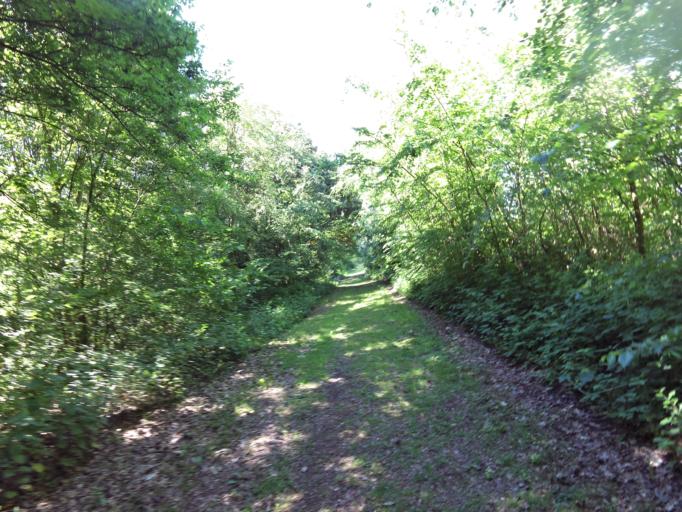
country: NL
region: South Holland
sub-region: Gemeente Goeree-Overflakkee
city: Goedereede
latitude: 51.8161
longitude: 4.0385
